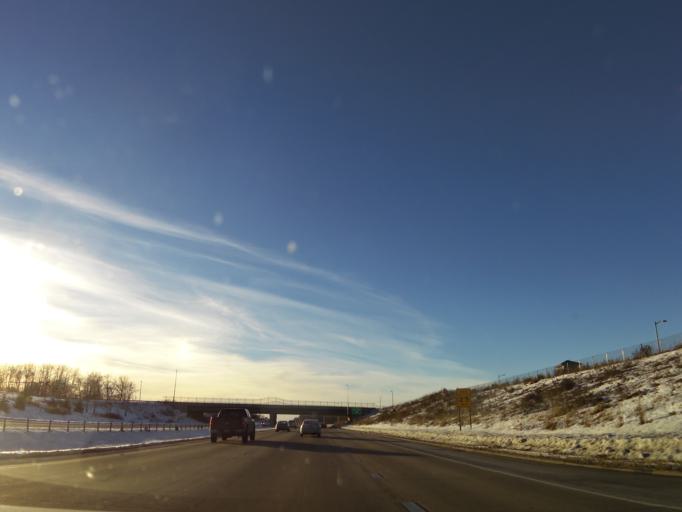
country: US
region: Minnesota
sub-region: Hennepin County
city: Eden Prairie
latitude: 44.8497
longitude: -93.5015
